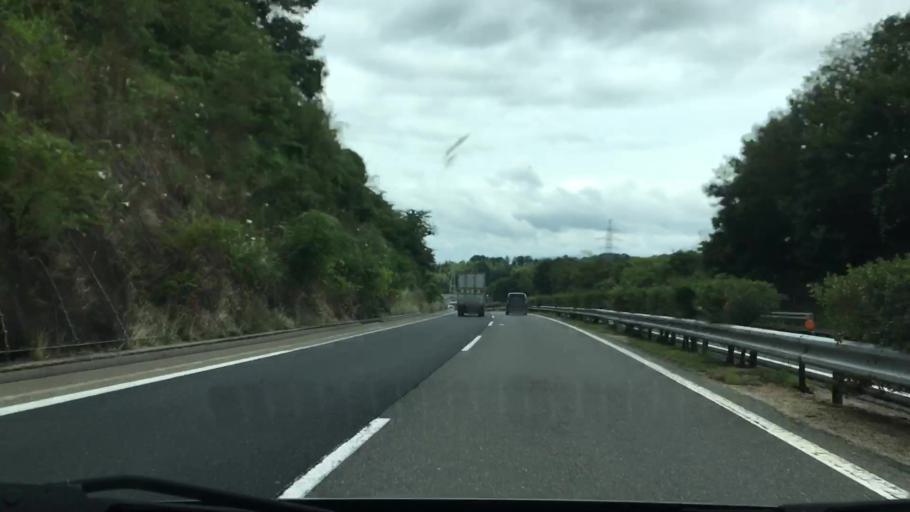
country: JP
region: Okayama
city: Tsuyama
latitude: 35.0650
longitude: 133.9694
